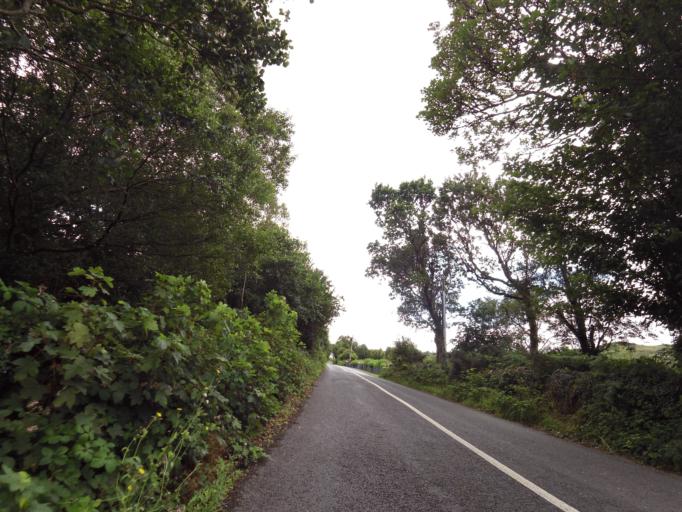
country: IE
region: Connaught
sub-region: County Galway
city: Oughterard
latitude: 53.4152
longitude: -9.3315
